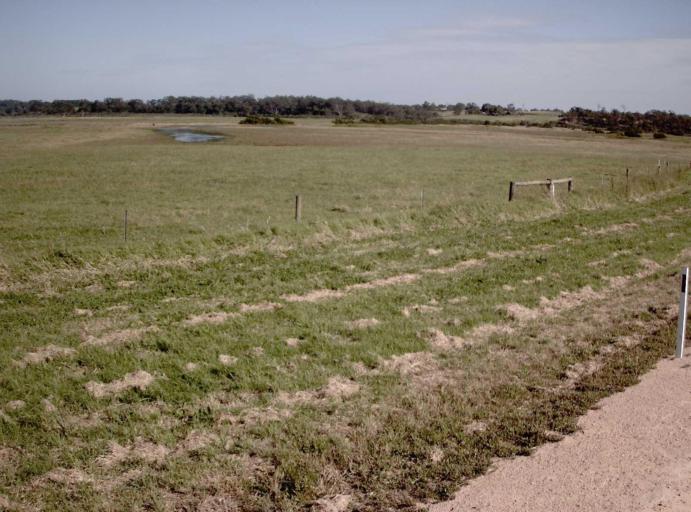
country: AU
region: Victoria
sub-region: East Gippsland
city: Lakes Entrance
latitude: -37.7695
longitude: 148.5367
